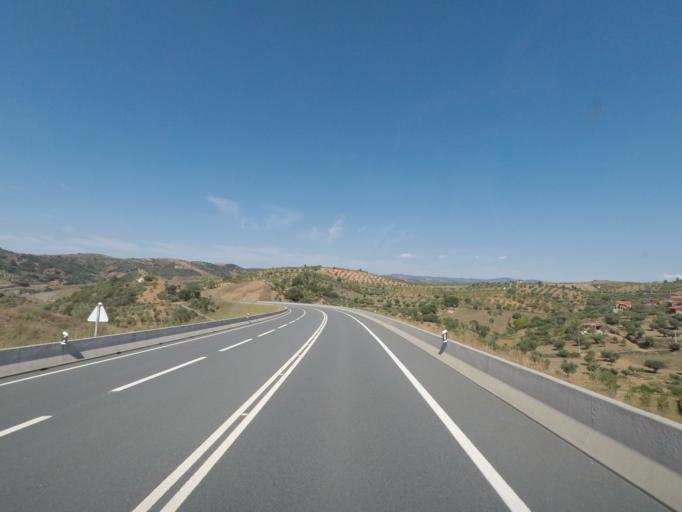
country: PT
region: Braganca
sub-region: Alfandega da Fe
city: Alfandega da Fe
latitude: 41.3067
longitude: -6.9069
